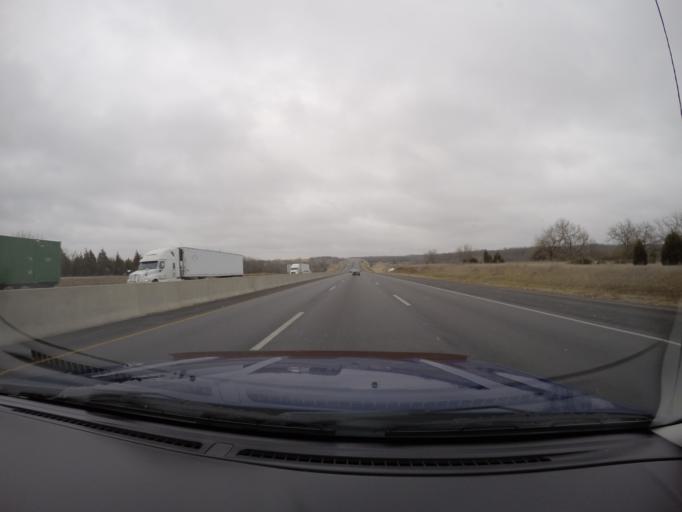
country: US
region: Kansas
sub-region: Shawnee County
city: Topeka
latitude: 39.0255
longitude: -95.5521
